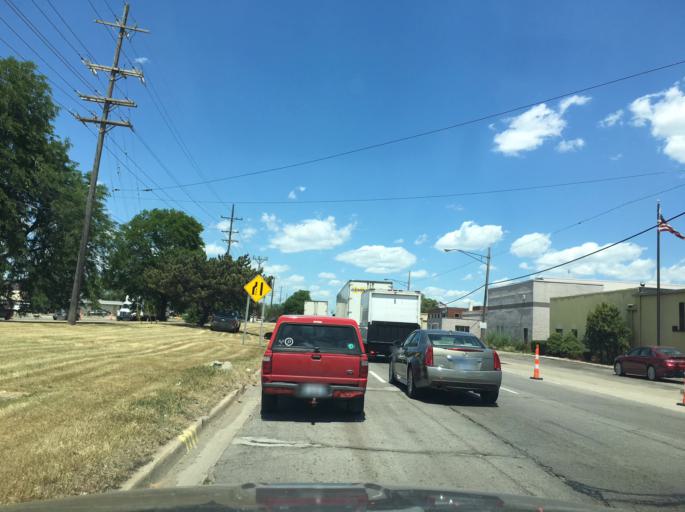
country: US
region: Michigan
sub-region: Macomb County
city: Warren
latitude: 42.4738
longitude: -83.0452
